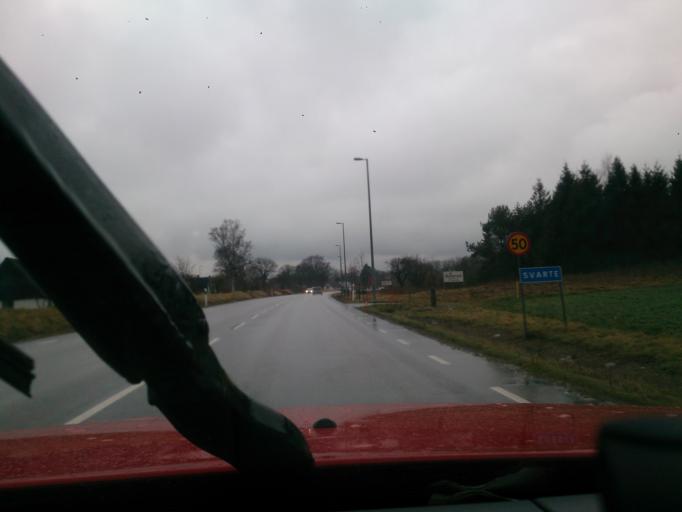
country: SE
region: Skane
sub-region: Ystads Kommun
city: Ystad
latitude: 55.4265
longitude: 13.7282
